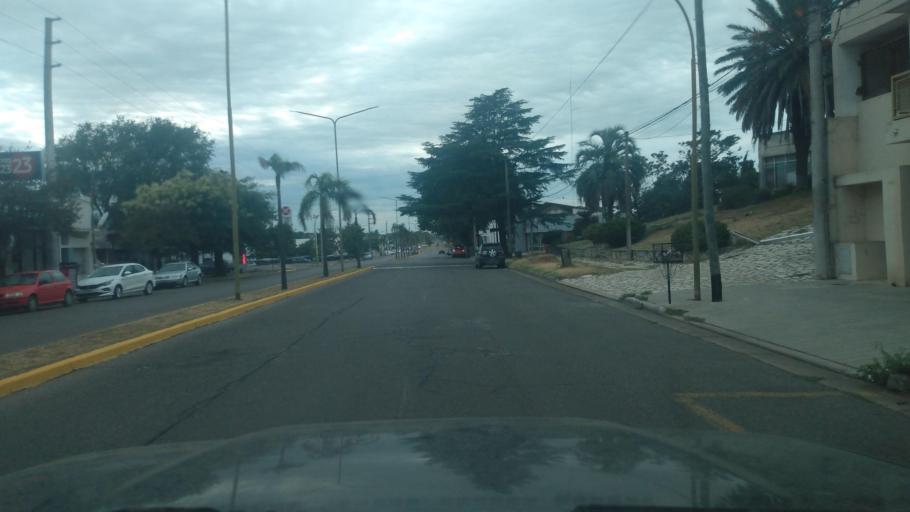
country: AR
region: Buenos Aires
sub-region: Partido de Trenque Lauquen
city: Trenque Lauquen
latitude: -35.9787
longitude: -62.7295
